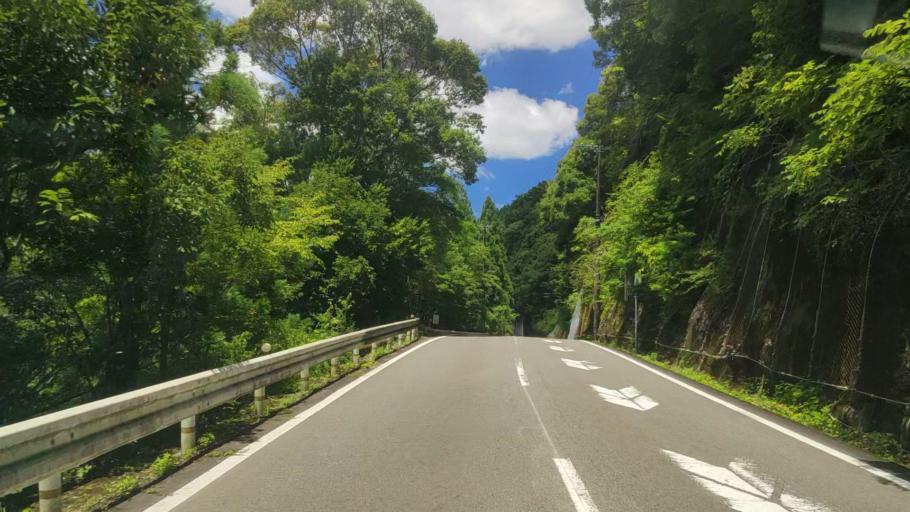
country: JP
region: Mie
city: Owase
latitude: 33.9963
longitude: 136.0128
